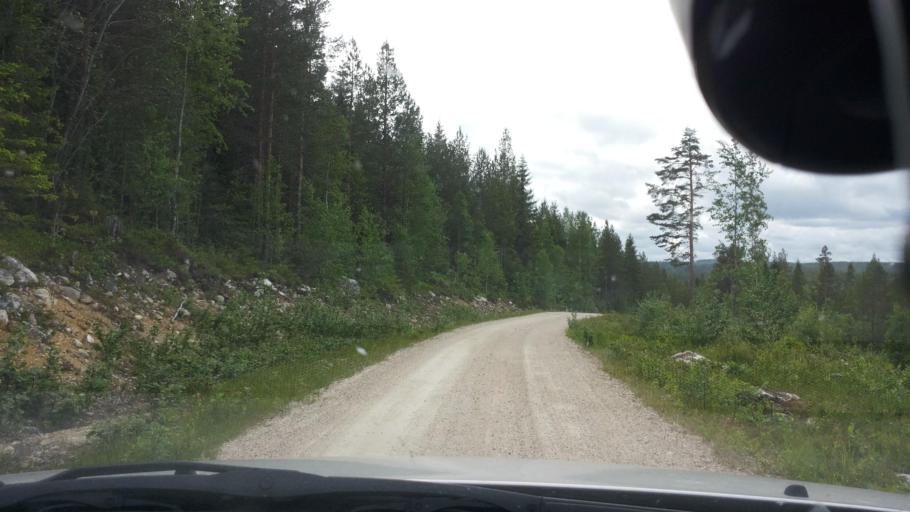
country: SE
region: Gaevleborg
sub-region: Ovanakers Kommun
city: Edsbyn
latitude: 61.4771
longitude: 15.3111
